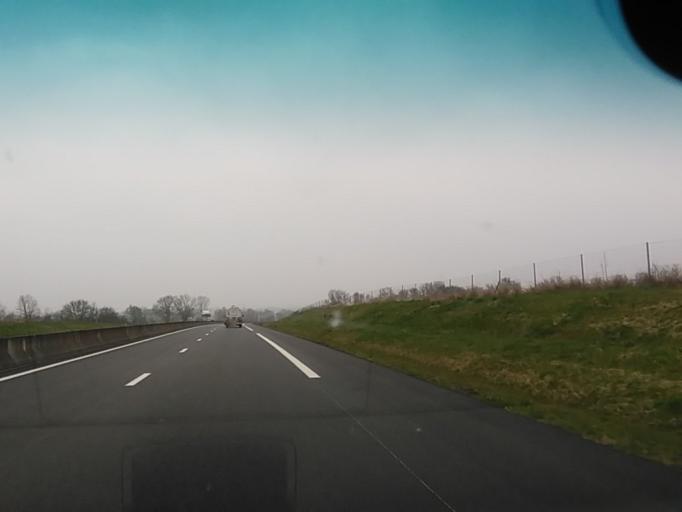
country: FR
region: Lower Normandy
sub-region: Departement de l'Orne
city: Gace
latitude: 48.7445
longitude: 0.2713
